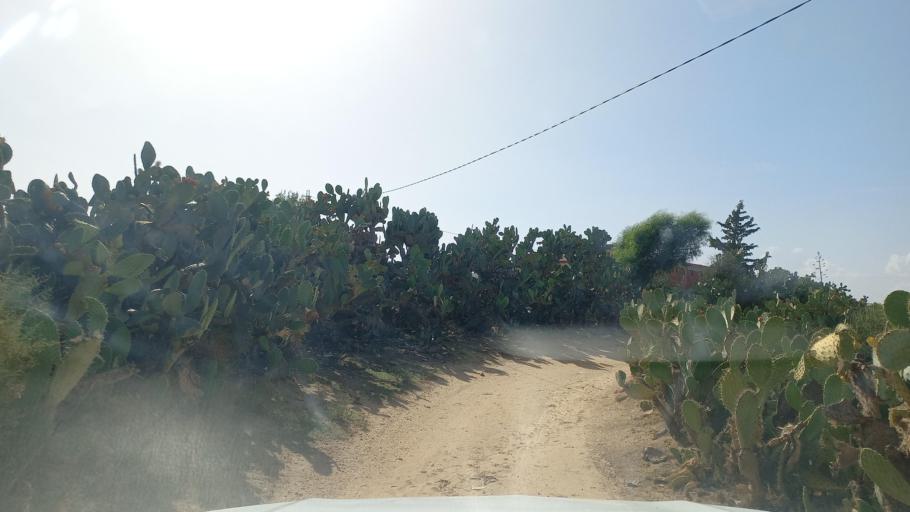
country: TN
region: Al Qasrayn
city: Sbiba
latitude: 35.3174
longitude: 9.0268
